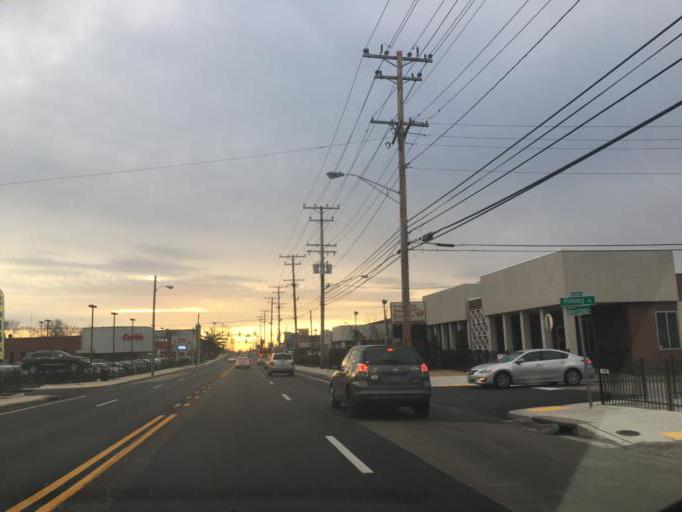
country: US
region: Maryland
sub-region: Baltimore County
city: Lochearn
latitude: 39.3528
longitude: -76.6977
